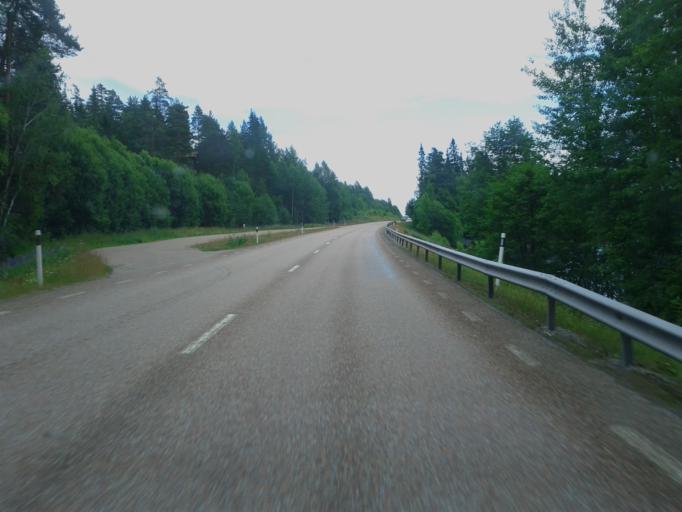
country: SE
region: Dalarna
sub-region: Faluns Kommun
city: Bjursas
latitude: 60.7586
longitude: 15.3333
